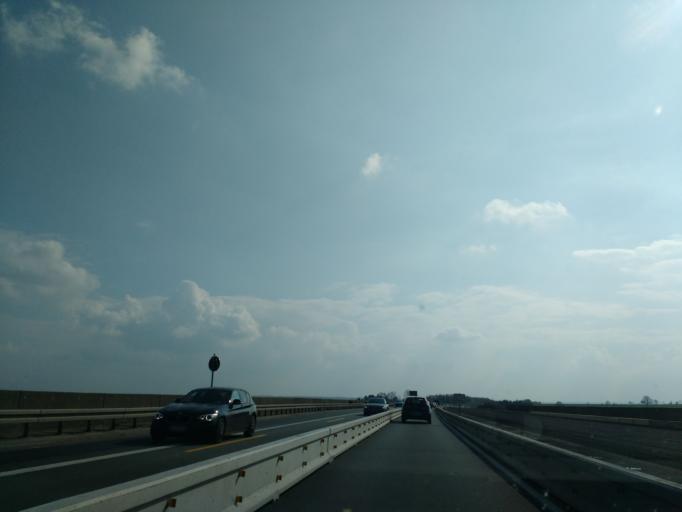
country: DE
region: North Rhine-Westphalia
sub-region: Regierungsbezirk Detmold
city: Paderborn
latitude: 51.6771
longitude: 8.7135
